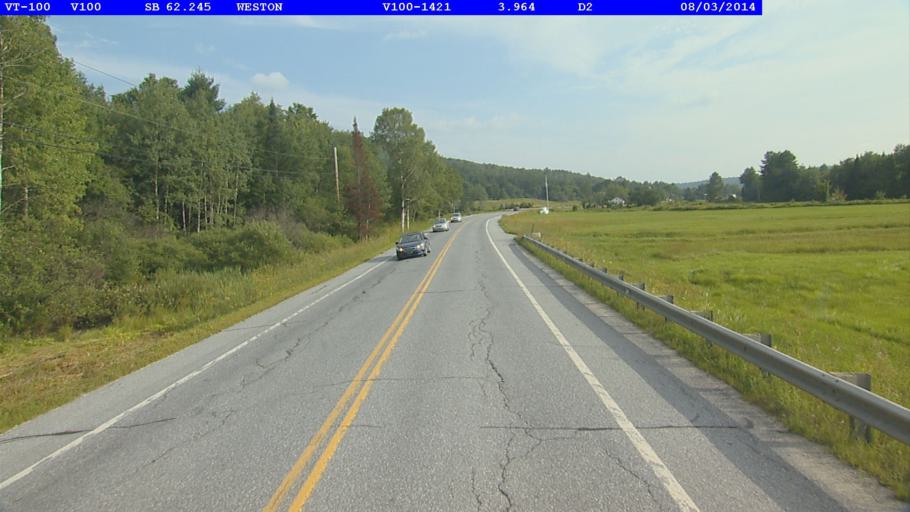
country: US
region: Vermont
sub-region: Windsor County
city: Chester
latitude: 43.3013
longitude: -72.7859
